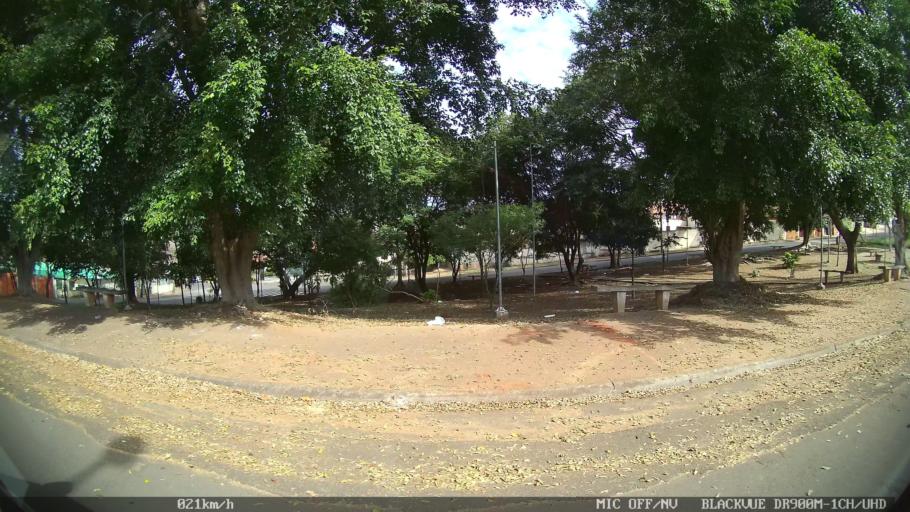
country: BR
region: Sao Paulo
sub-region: Santa Barbara D'Oeste
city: Santa Barbara d'Oeste
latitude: -22.7603
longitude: -47.4208
